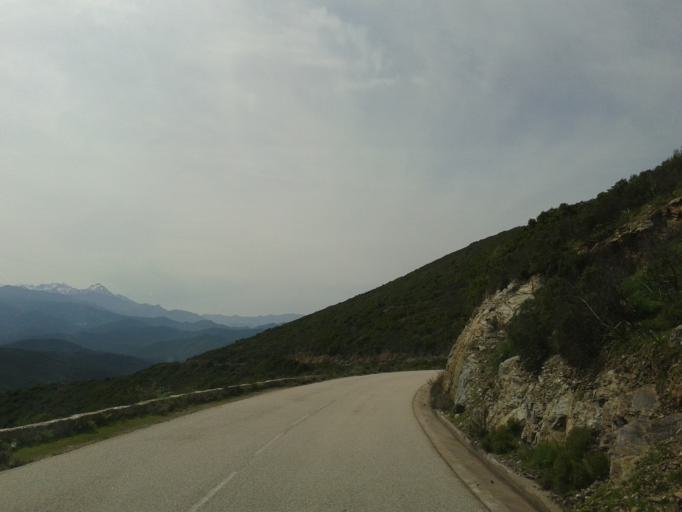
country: FR
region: Corsica
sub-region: Departement de la Haute-Corse
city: Saint-Florent
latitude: 42.6655
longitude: 9.1401
